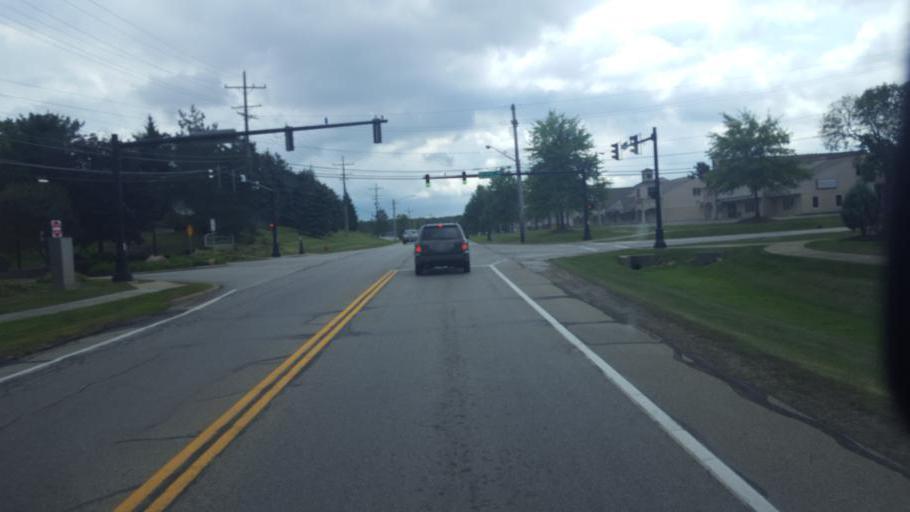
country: US
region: Ohio
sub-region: Geauga County
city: Chardon
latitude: 41.5628
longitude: -81.2005
